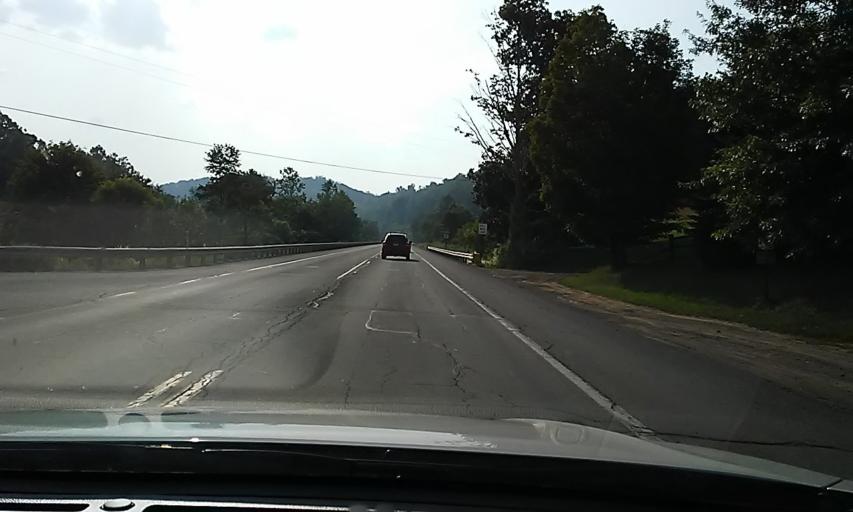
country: US
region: Pennsylvania
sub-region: McKean County
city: Port Allegany
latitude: 41.7906
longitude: -78.1786
